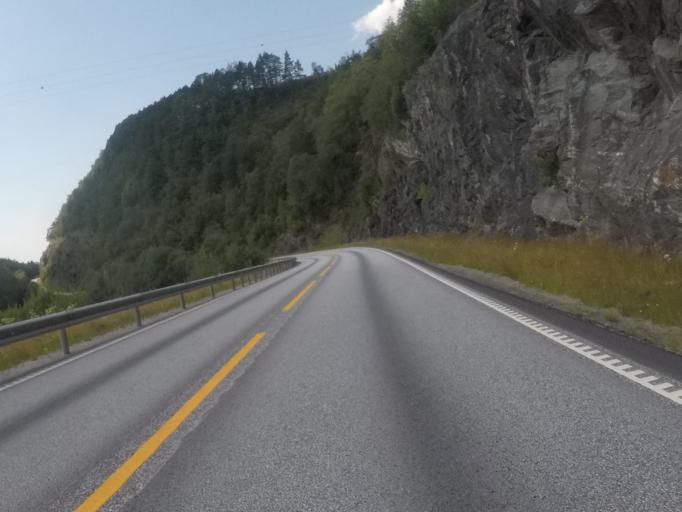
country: NO
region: Sogn og Fjordane
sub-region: Bremanger
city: Svelgen
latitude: 61.6118
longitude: 5.3181
